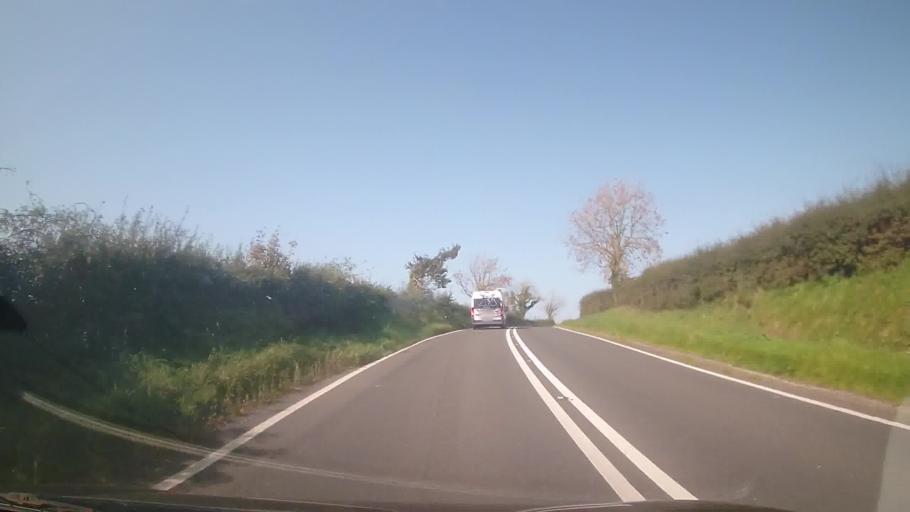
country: GB
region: Wales
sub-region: County of Ceredigion
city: Cardigan
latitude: 52.0377
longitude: -4.6970
